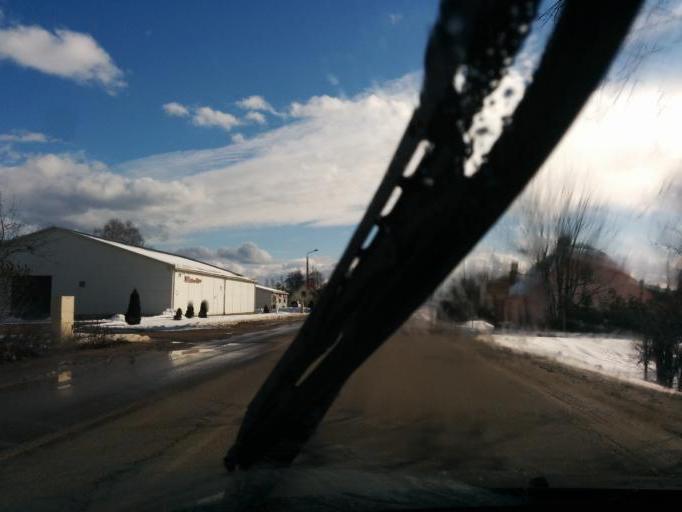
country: LV
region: Gulbenes Rajons
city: Gulbene
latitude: 57.1786
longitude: 26.7422
